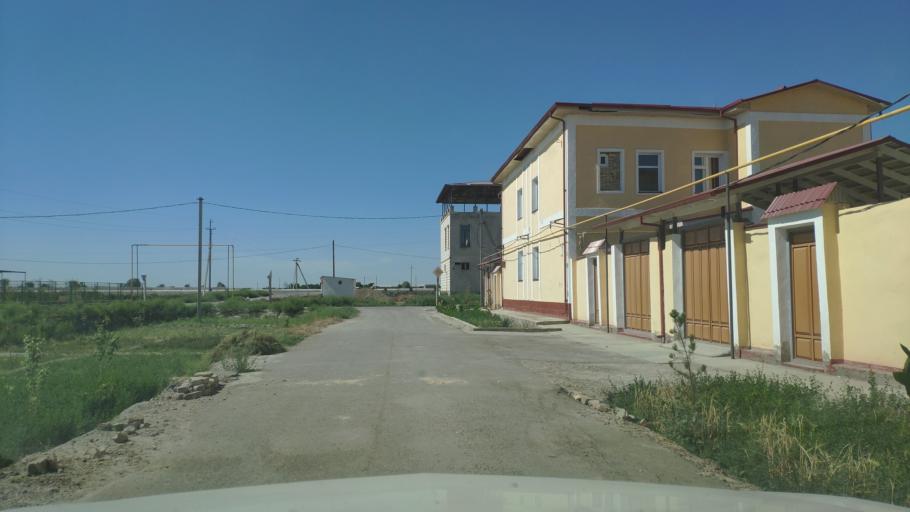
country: UZ
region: Bukhara
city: Bukhara
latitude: 39.7697
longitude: 64.3749
